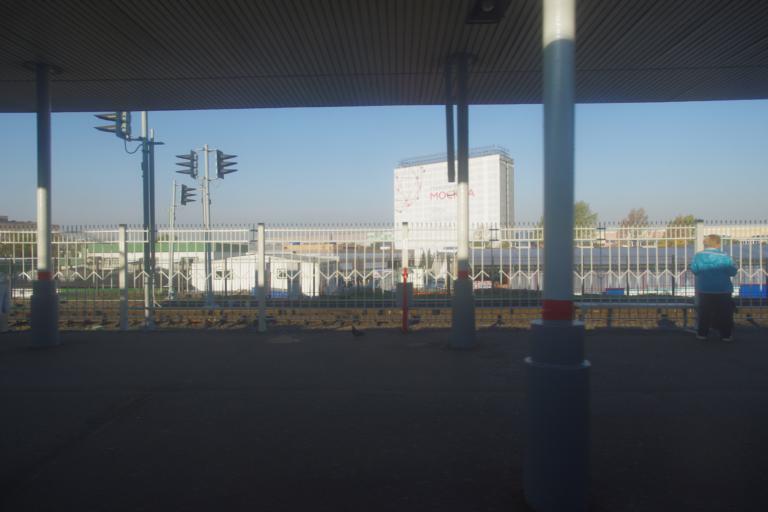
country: RU
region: Moscow
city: Tekstil'shchiki
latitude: 55.7065
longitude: 37.7297
